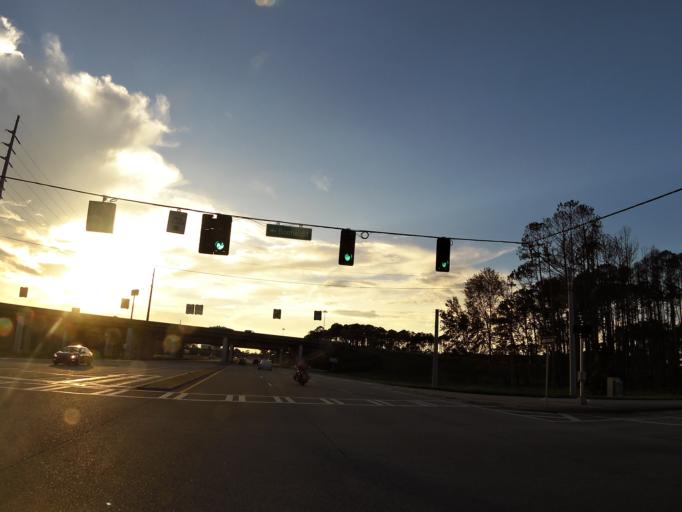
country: US
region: Georgia
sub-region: Camden County
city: Kingsland
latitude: 30.7902
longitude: -81.6573
